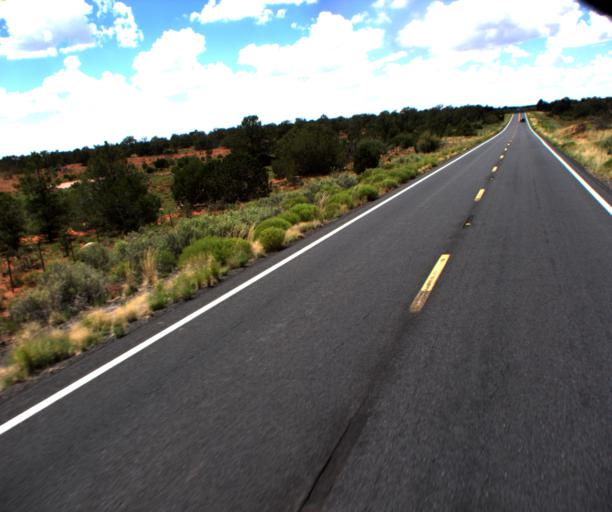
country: US
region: Arizona
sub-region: Coconino County
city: Parks
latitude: 35.6010
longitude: -112.0273
